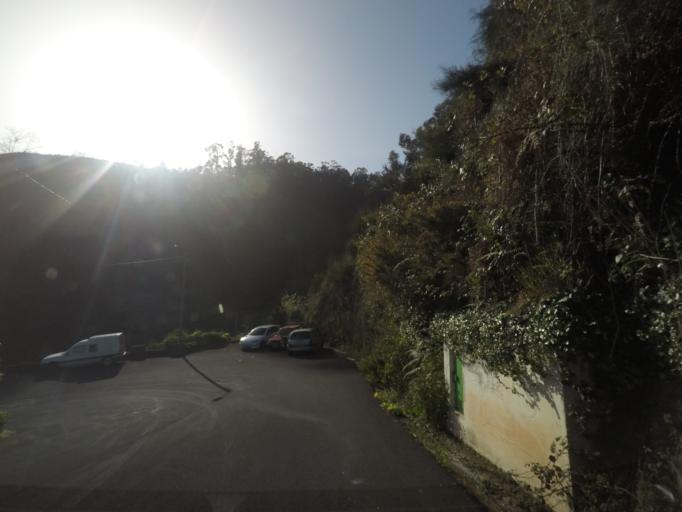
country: PT
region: Madeira
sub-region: Ribeira Brava
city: Campanario
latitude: 32.6748
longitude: -17.0067
